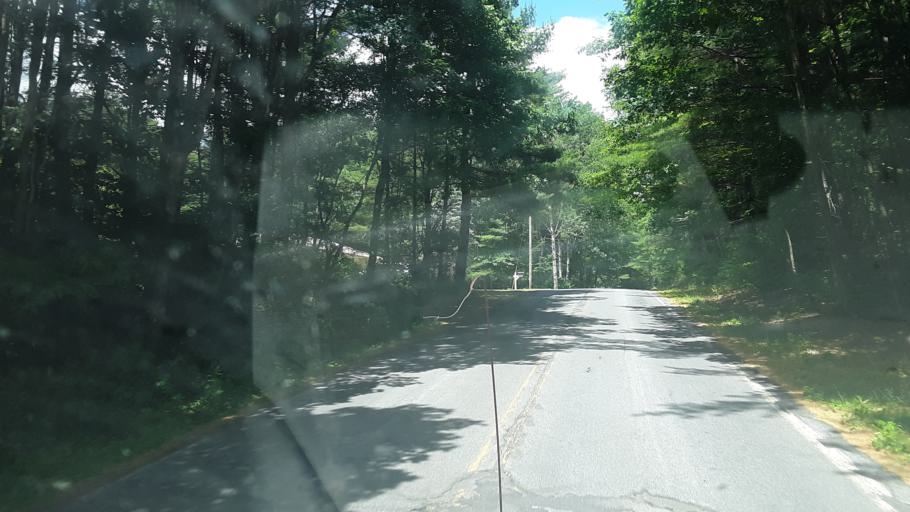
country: US
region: New York
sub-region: Oneida County
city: Rome
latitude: 43.2372
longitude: -75.5974
